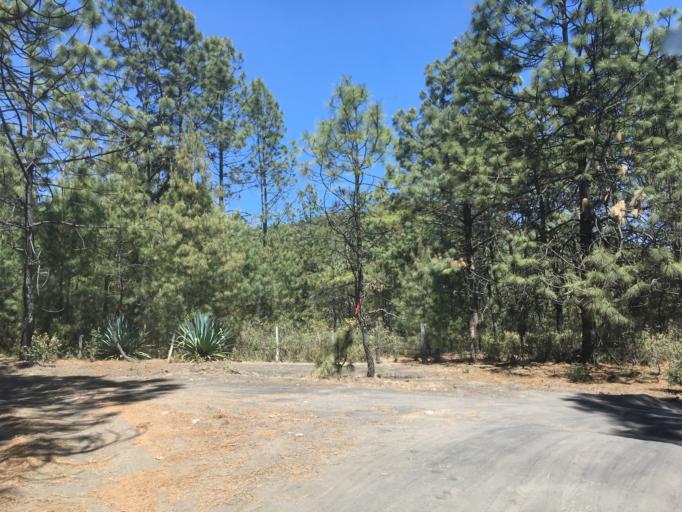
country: MX
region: Michoacan
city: Angahuan
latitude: 19.4606
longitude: -102.2391
